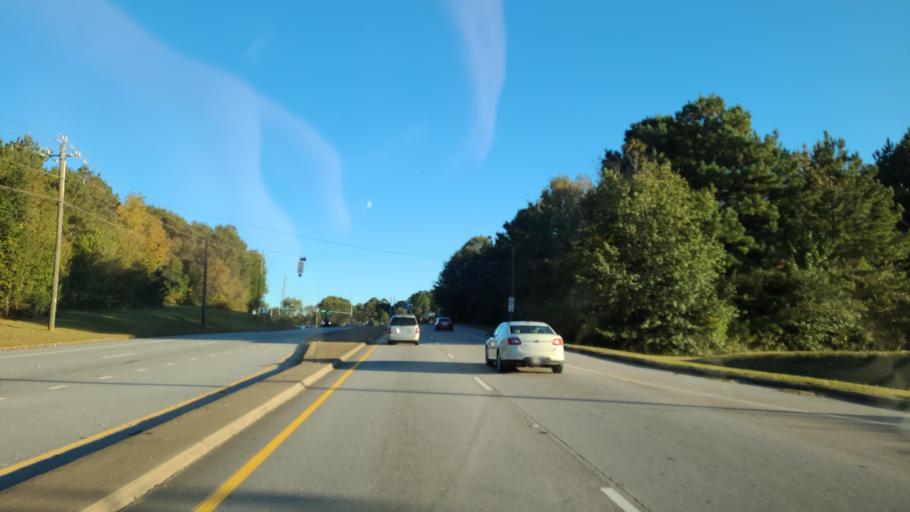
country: US
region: Georgia
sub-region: Clayton County
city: Morrow
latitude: 33.5794
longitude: -84.2890
